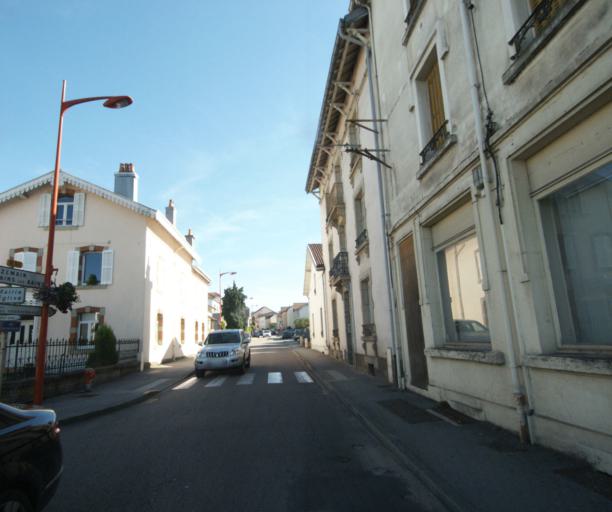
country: FR
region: Lorraine
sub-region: Departement des Vosges
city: Chantraine
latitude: 48.1743
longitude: 6.4340
